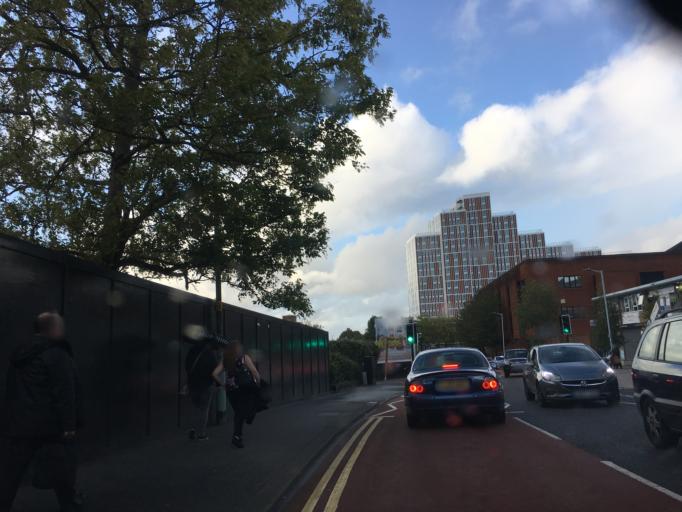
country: GB
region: England
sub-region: Bracknell Forest
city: Bracknell
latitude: 51.4152
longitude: -0.7529
